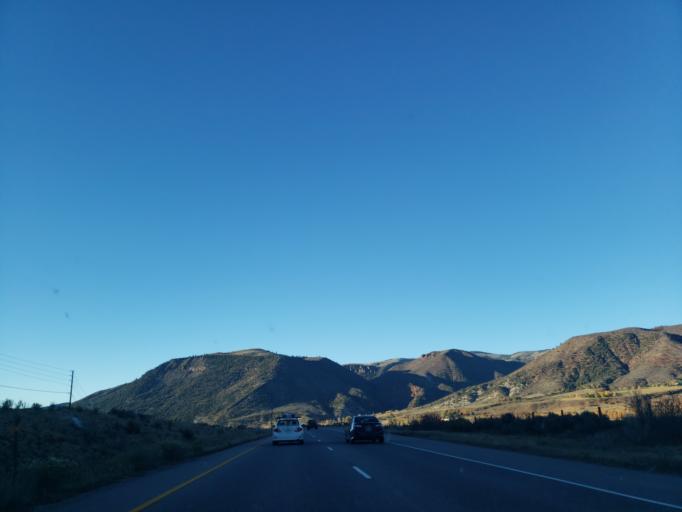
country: US
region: Colorado
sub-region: Pitkin County
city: Snowmass Village
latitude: 39.2734
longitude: -106.8921
